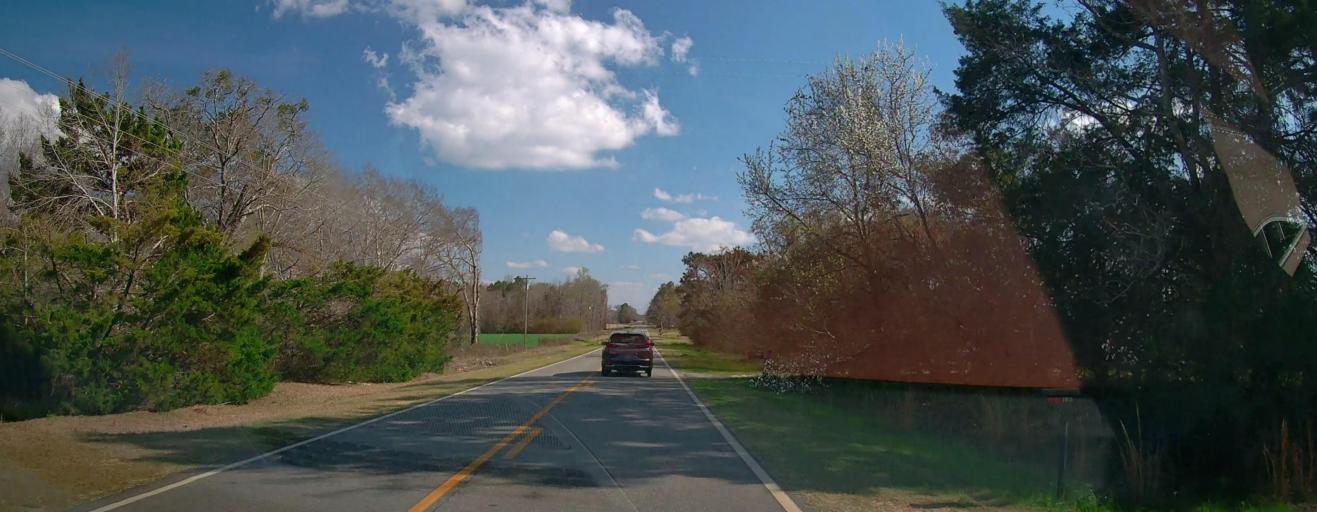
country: US
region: Georgia
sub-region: Laurens County
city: Dublin
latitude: 32.6170
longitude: -83.0854
